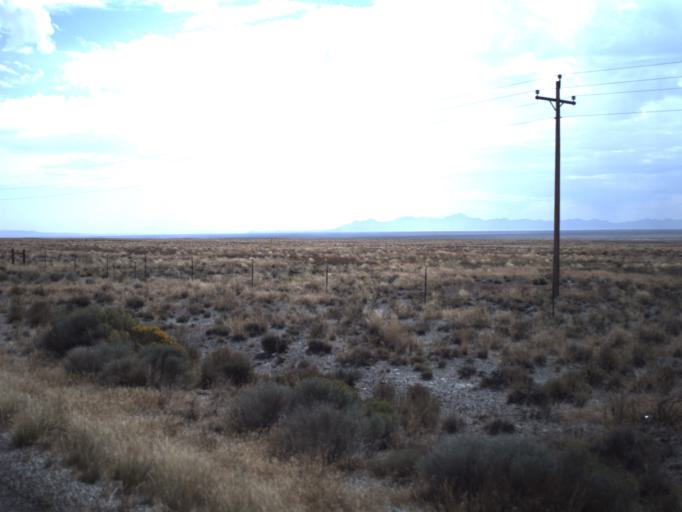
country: US
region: Utah
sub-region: Tooele County
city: Wendover
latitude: 41.4308
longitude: -113.8011
